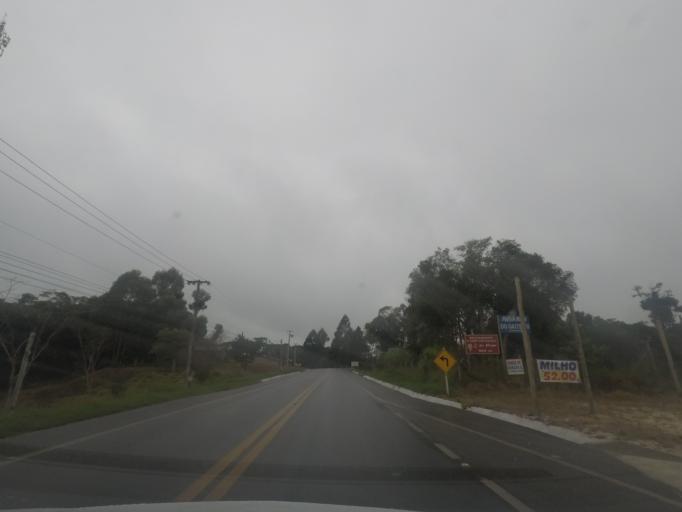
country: BR
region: Parana
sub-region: Colombo
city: Colombo
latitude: -25.3132
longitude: -49.1478
